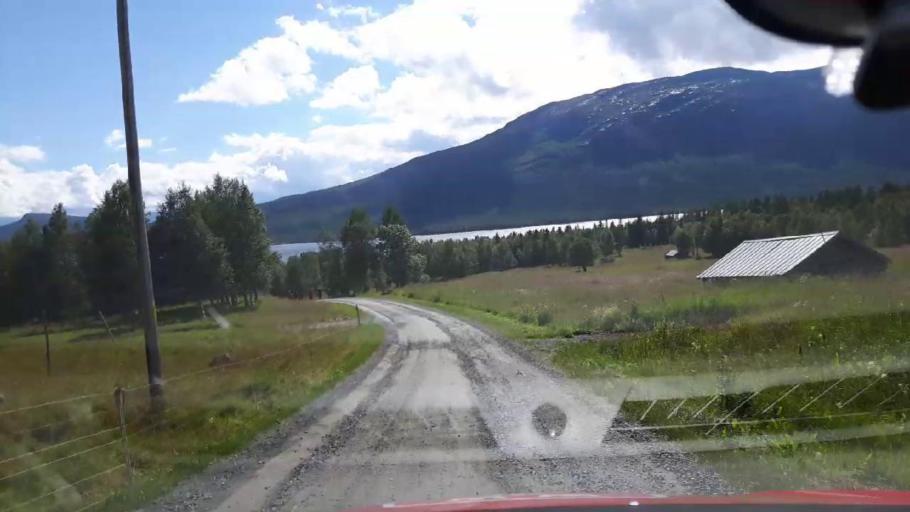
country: SE
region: Jaemtland
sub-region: Are Kommun
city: Are
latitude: 63.2149
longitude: 13.0551
